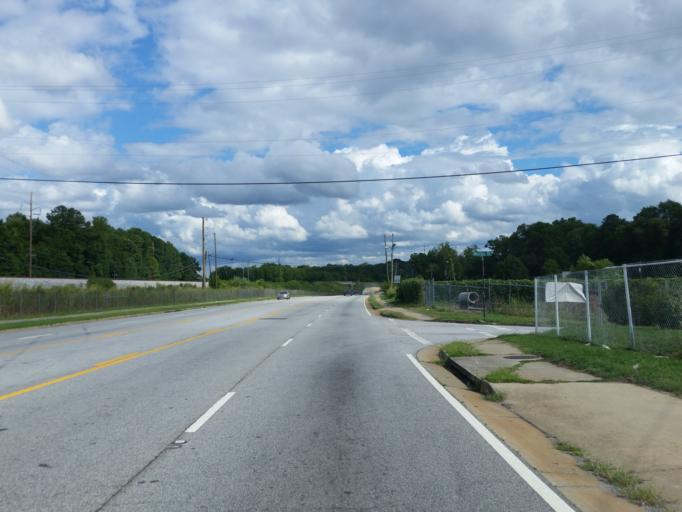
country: US
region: Georgia
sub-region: Cobb County
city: Fair Oaks
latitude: 33.9094
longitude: -84.5311
